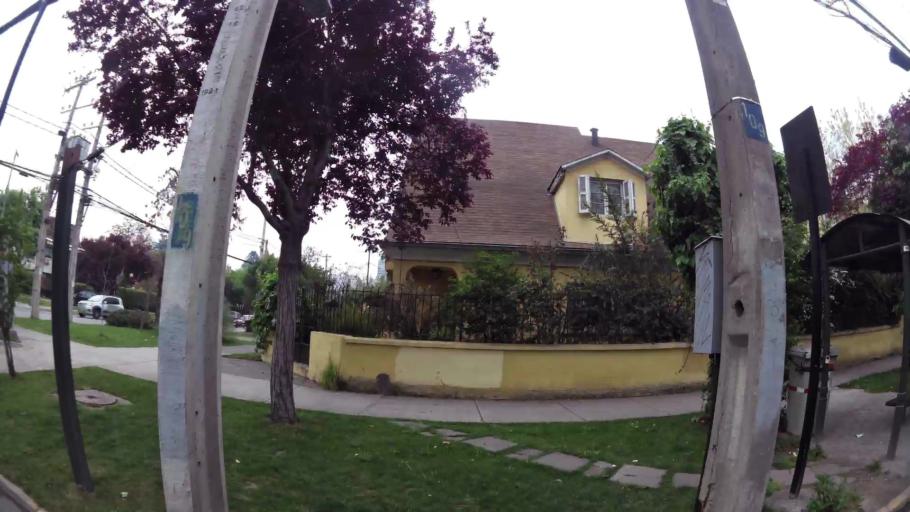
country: CL
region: Santiago Metropolitan
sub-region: Provincia de Santiago
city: Villa Presidente Frei, Nunoa, Santiago, Chile
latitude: -33.4596
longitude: -70.5867
